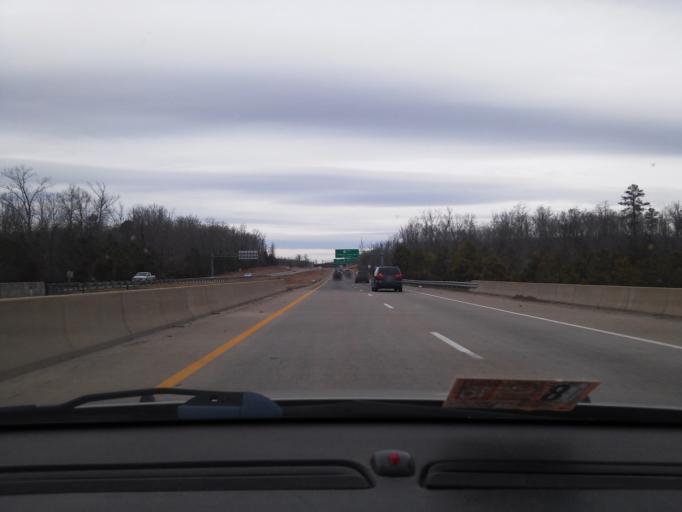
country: US
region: Virginia
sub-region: Henrico County
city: Short Pump
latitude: 37.6212
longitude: -77.6636
